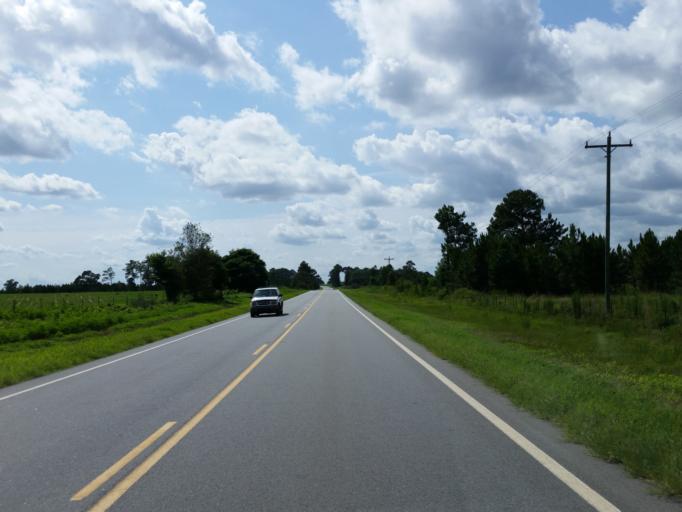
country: US
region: Georgia
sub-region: Turner County
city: Ashburn
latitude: 31.6542
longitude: -83.5537
